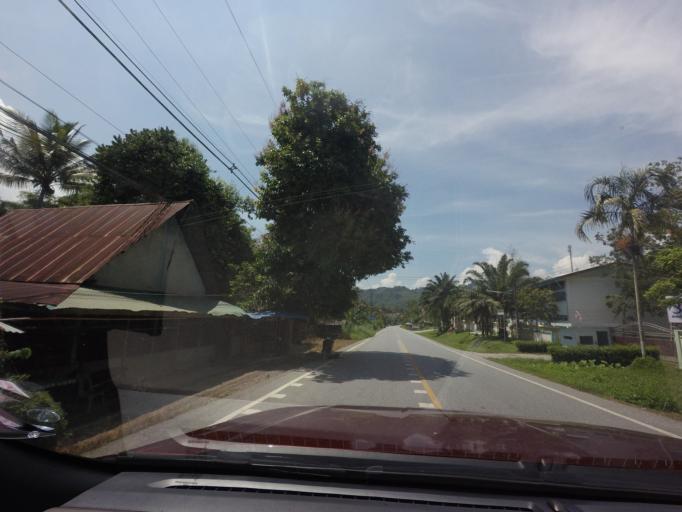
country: TH
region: Yala
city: Betong
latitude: 5.9179
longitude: 101.1765
